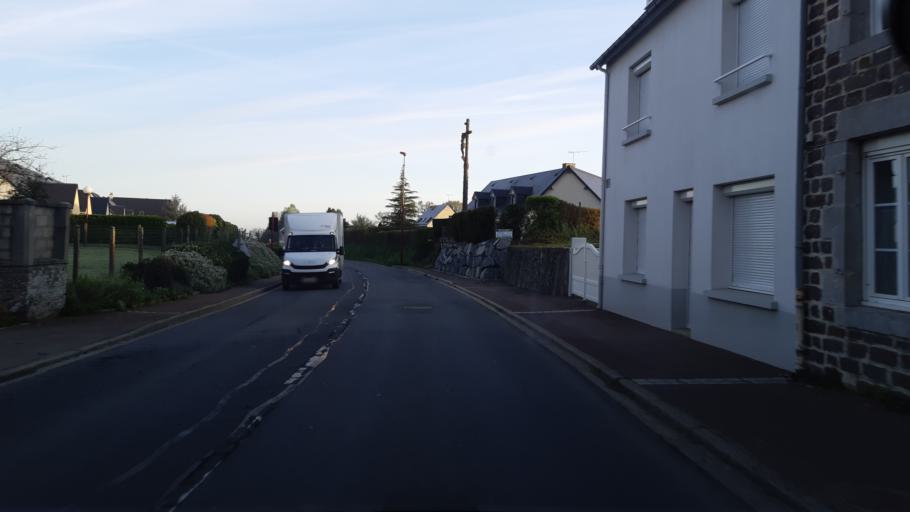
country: FR
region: Lower Normandy
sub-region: Departement de la Manche
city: Agneaux
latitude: 49.0504
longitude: -1.1287
